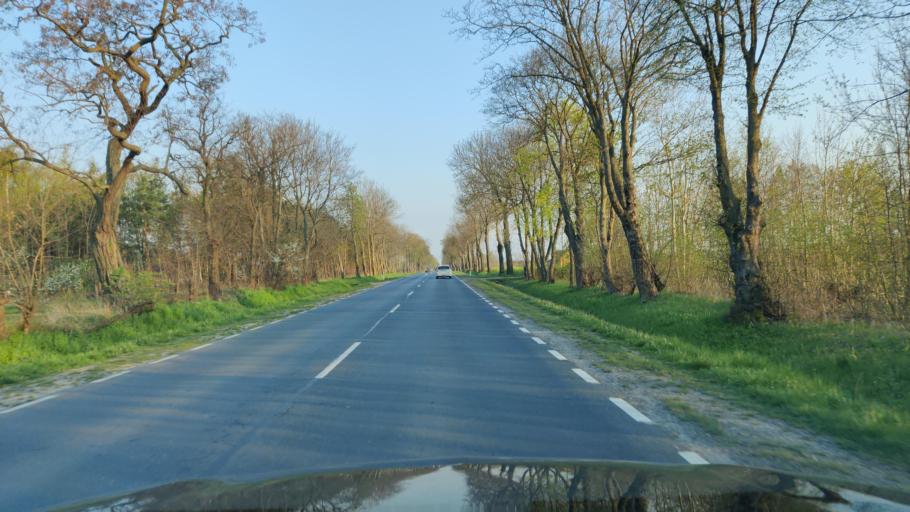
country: PL
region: Masovian Voivodeship
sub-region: Powiat pultuski
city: Pultusk
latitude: 52.6404
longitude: 21.0932
